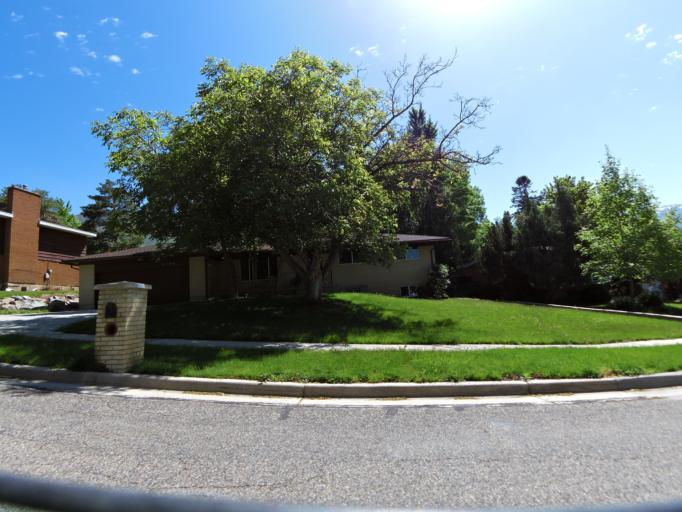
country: US
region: Utah
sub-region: Weber County
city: Uintah
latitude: 41.1695
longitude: -111.9390
